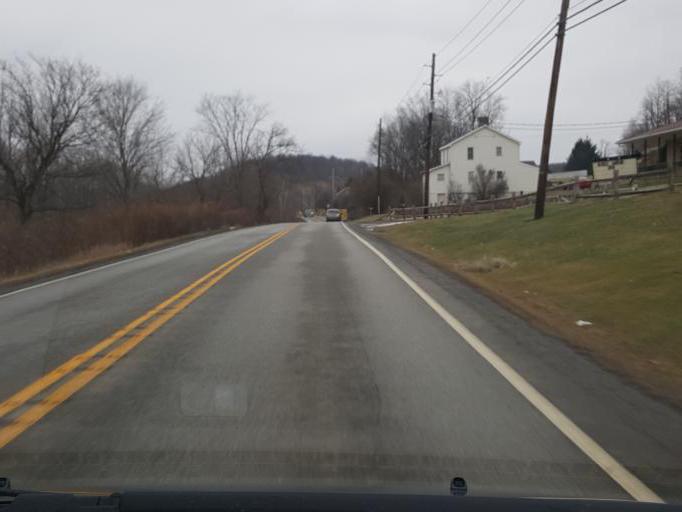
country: US
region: Pennsylvania
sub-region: Blair County
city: Greenwood
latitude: 40.5636
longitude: -78.3554
